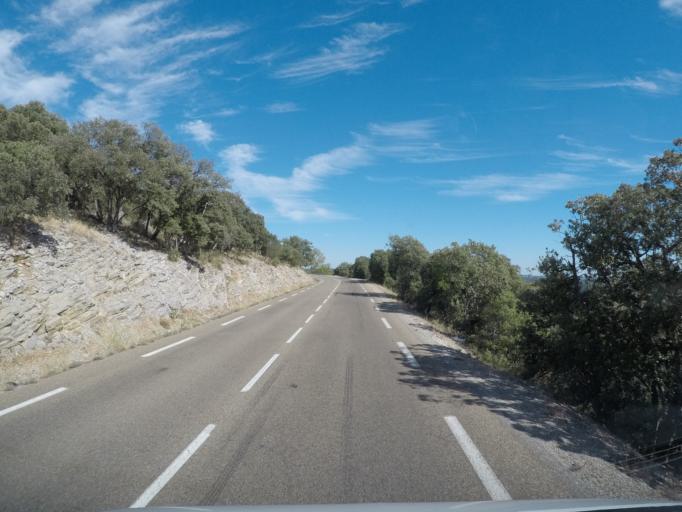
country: FR
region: Languedoc-Roussillon
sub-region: Departement du Gard
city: Sauve
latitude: 43.9602
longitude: 3.9064
